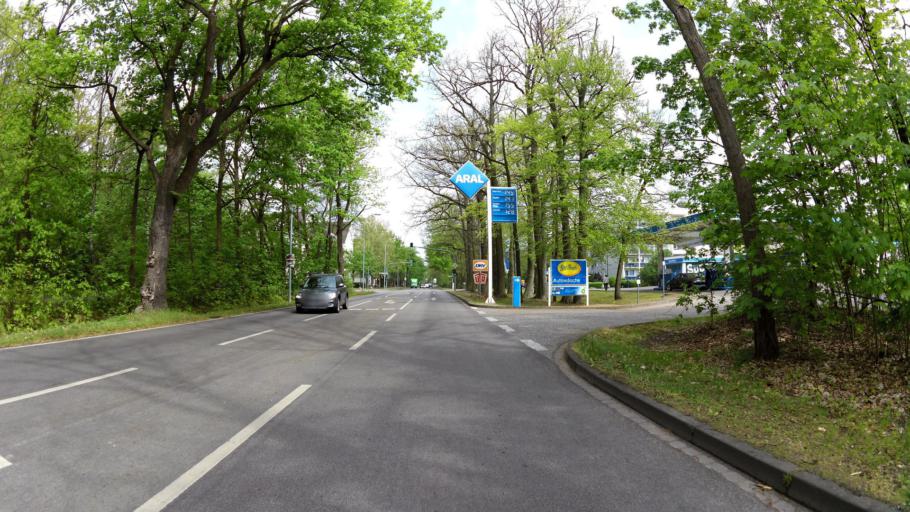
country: DE
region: Brandenburg
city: Konigs Wusterhausen
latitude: 52.2837
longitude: 13.6141
